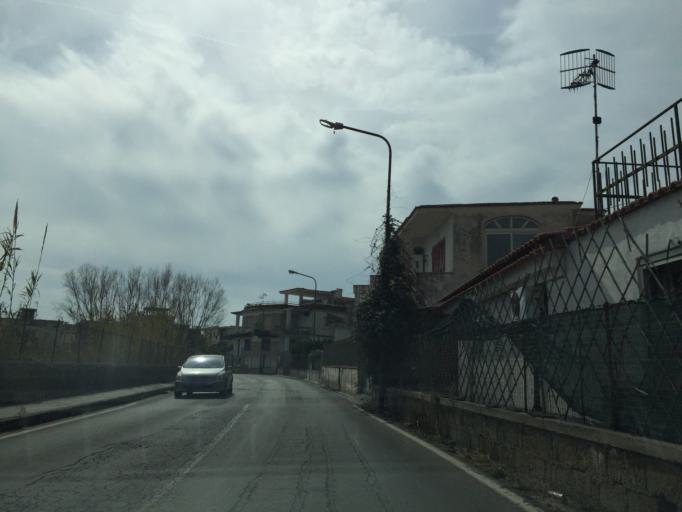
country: IT
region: Campania
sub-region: Provincia di Napoli
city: Bacoli
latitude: 40.7916
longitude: 14.0663
